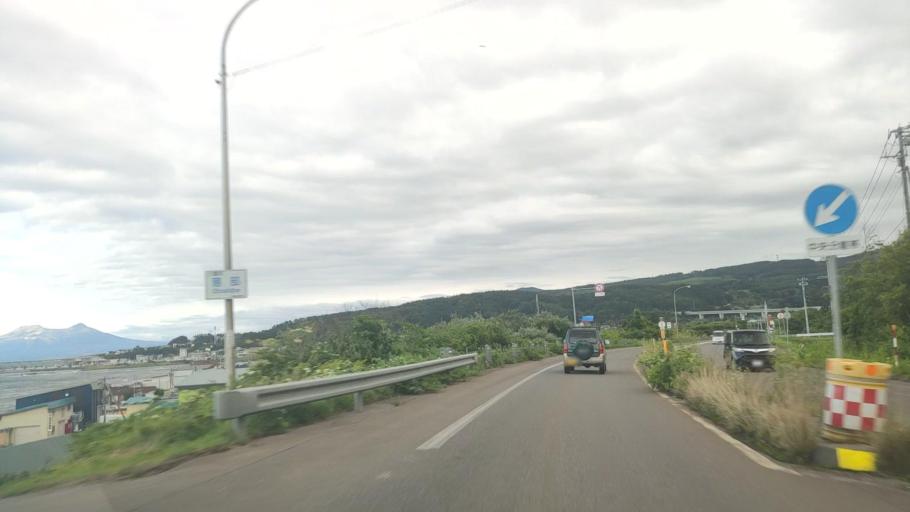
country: JP
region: Hokkaido
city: Nanae
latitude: 42.1971
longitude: 140.4196
